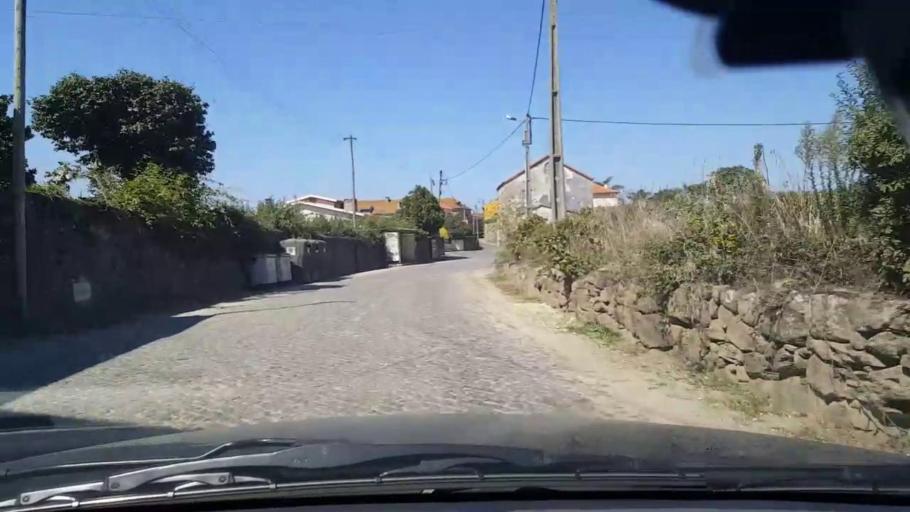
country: PT
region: Porto
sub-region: Matosinhos
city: Lavra
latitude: 41.2763
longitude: -8.7087
